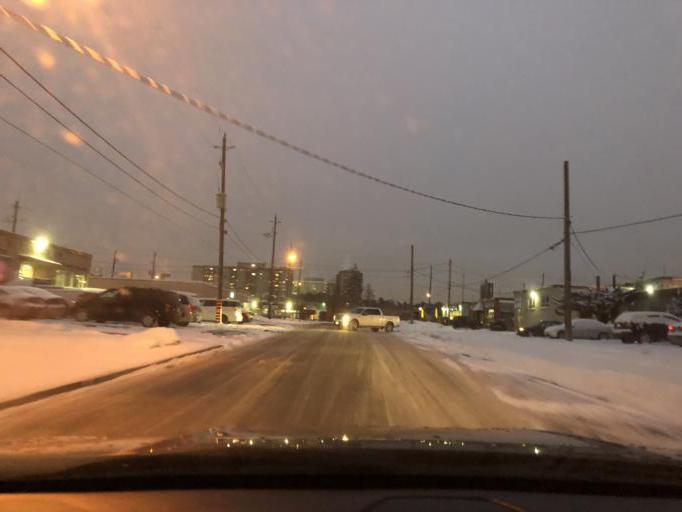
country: CA
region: Ontario
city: Toronto
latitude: 43.7047
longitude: -79.4723
